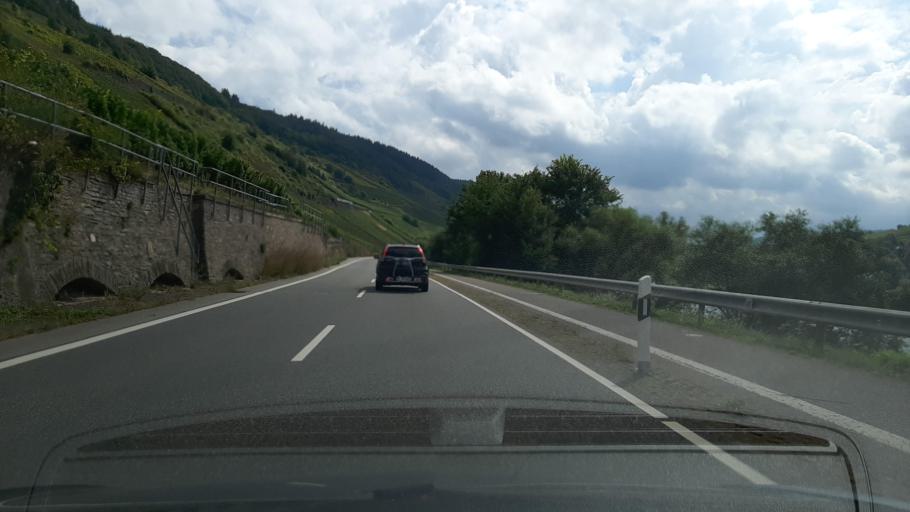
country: DE
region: Rheinland-Pfalz
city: Reil
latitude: 50.0206
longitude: 7.1210
